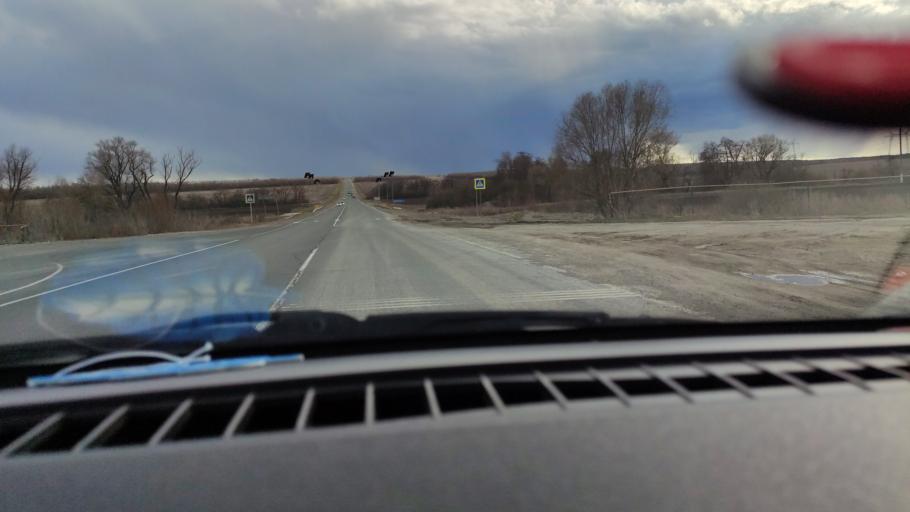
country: RU
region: Saratov
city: Sinodskoye
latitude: 51.9181
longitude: 46.5588
